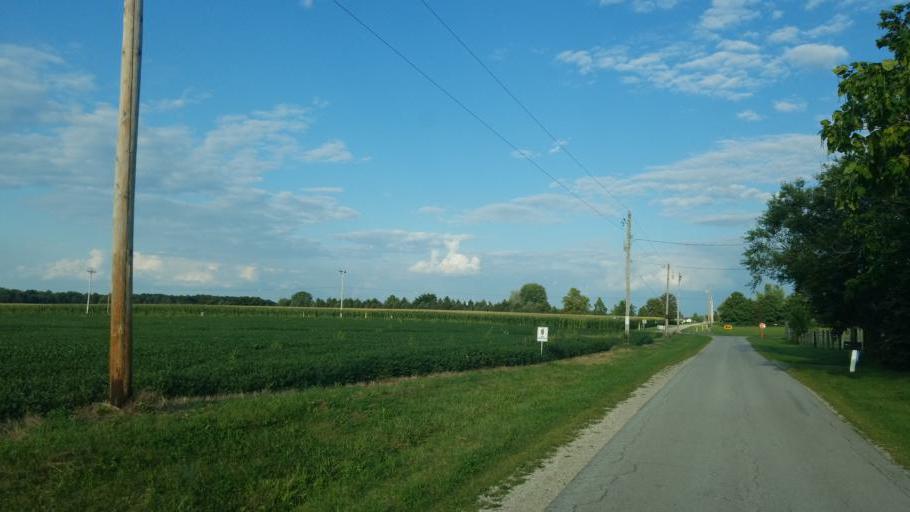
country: US
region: Ohio
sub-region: Sandusky County
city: Mount Carmel
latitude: 41.1102
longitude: -82.9590
